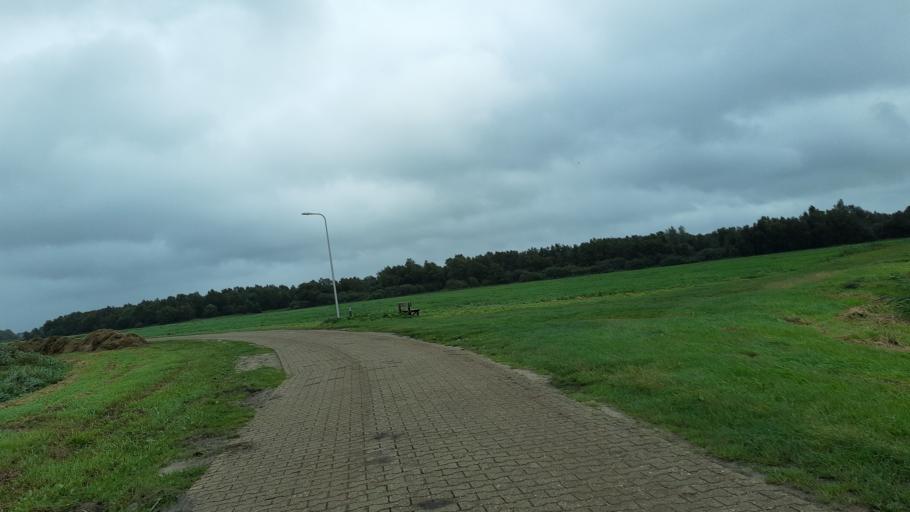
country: NL
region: Overijssel
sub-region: Gemeente Steenwijkerland
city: Blokzijl
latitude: 52.7547
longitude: 5.9781
